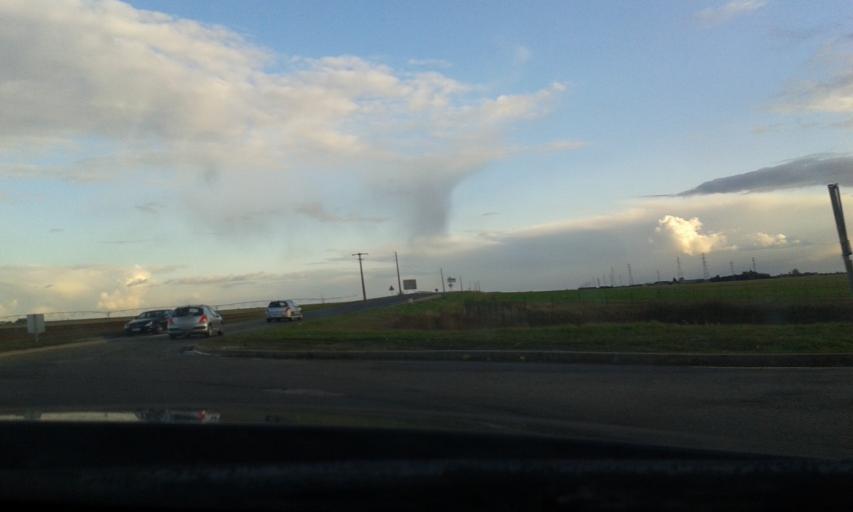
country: FR
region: Centre
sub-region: Departement d'Eure-et-Loir
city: Voves
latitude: 48.3142
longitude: 1.6785
